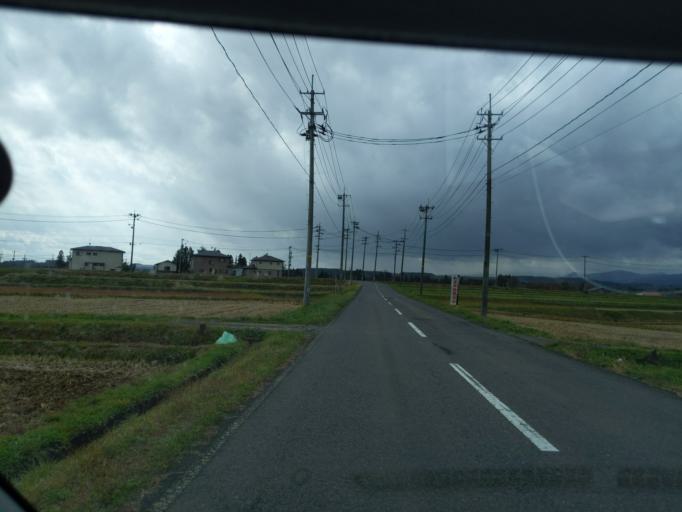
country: JP
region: Iwate
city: Mizusawa
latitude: 39.0579
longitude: 141.1160
